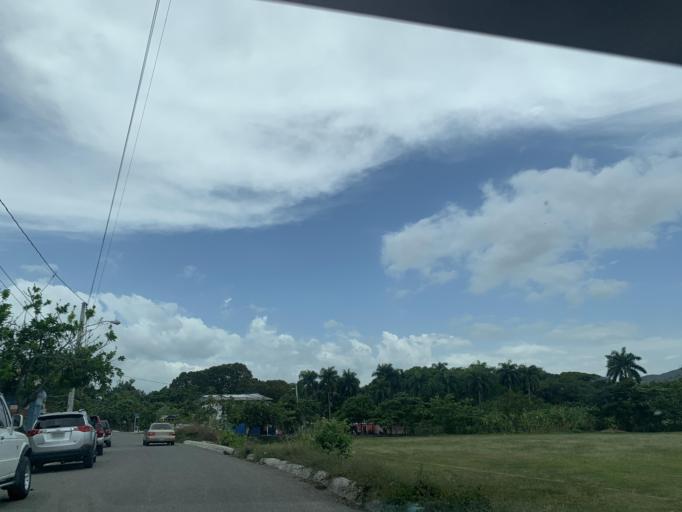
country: DO
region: Puerto Plata
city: Imbert
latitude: 19.8223
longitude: -70.7775
